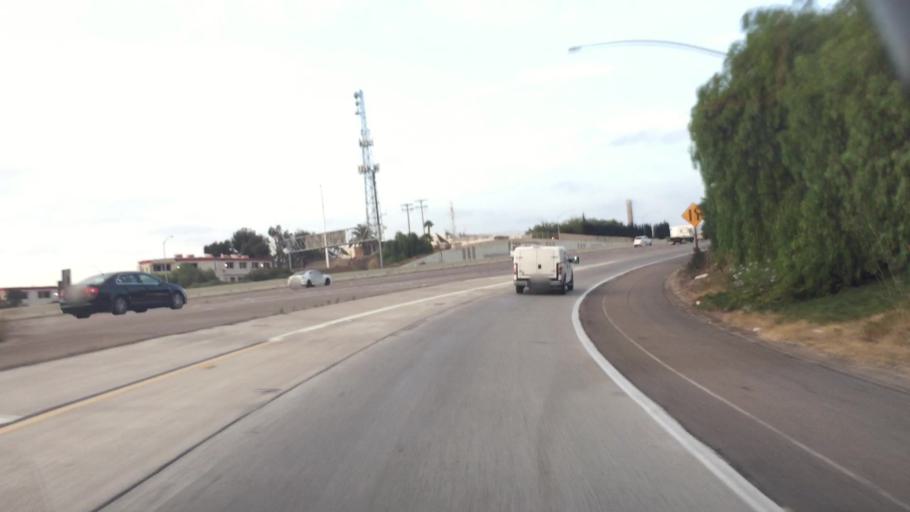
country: US
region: California
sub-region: San Diego County
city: National City
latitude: 32.7186
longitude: -117.1010
